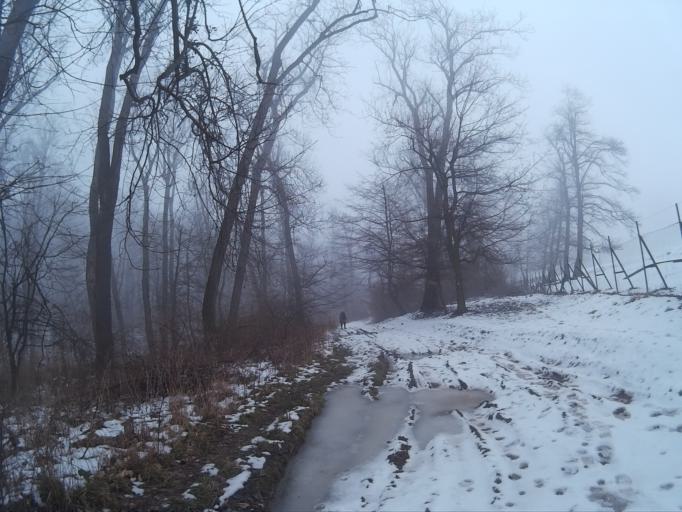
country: HU
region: Komarom-Esztergom
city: Tardos
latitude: 47.6856
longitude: 18.4924
